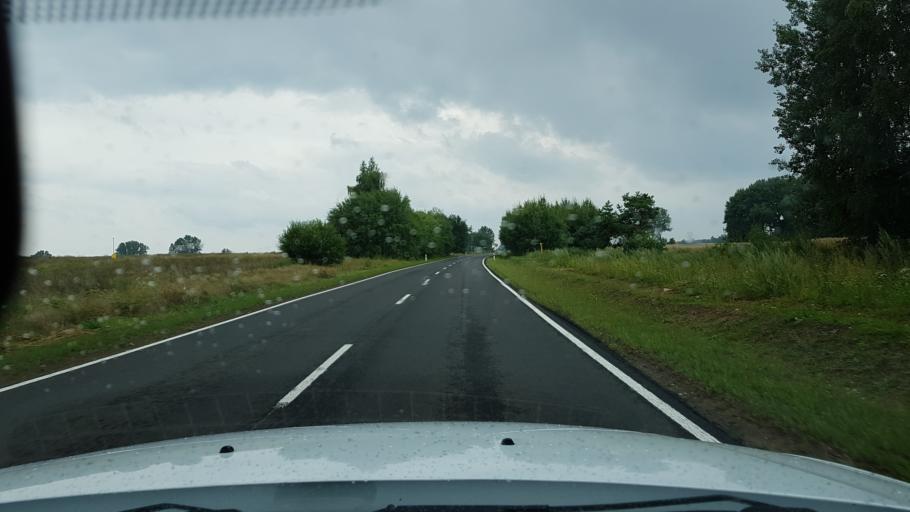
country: PL
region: West Pomeranian Voivodeship
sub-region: Powiat goleniowski
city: Maszewo
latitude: 53.4290
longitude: 14.9773
